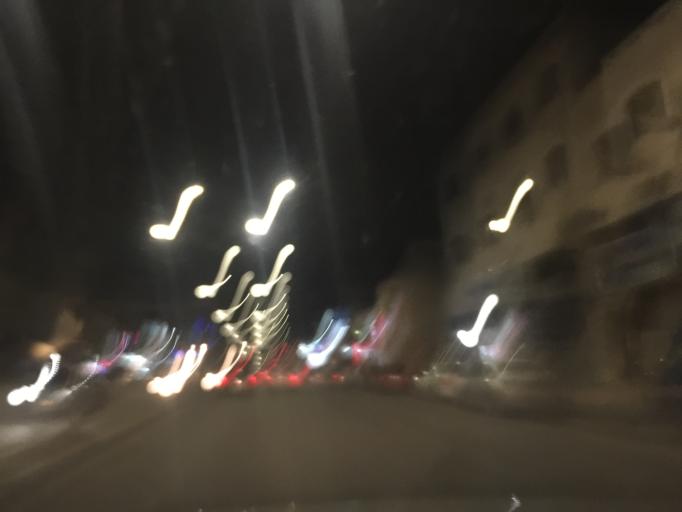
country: JO
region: Zarqa
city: Russeifa
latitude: 32.0266
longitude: 36.0532
